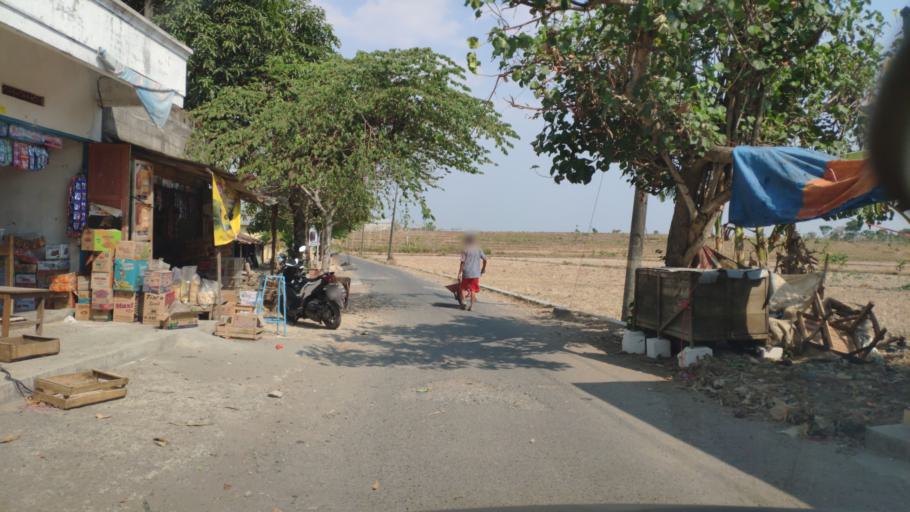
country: ID
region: Central Java
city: Pelem
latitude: -7.0017
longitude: 111.4333
